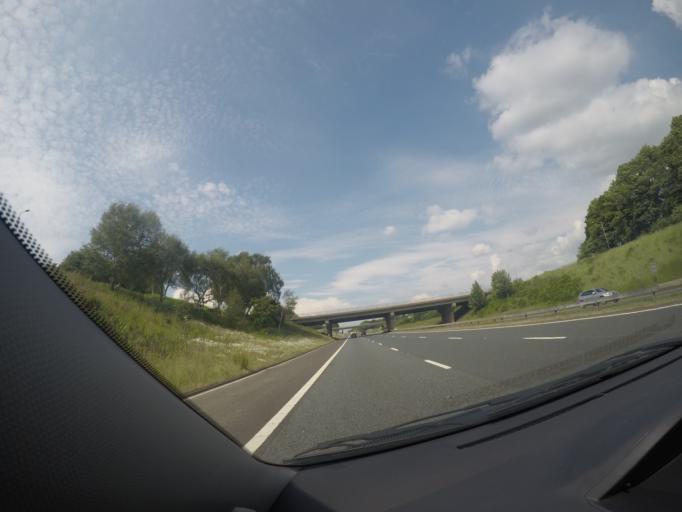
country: GB
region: England
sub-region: Cumbria
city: Scotby
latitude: 54.8560
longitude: -2.8791
